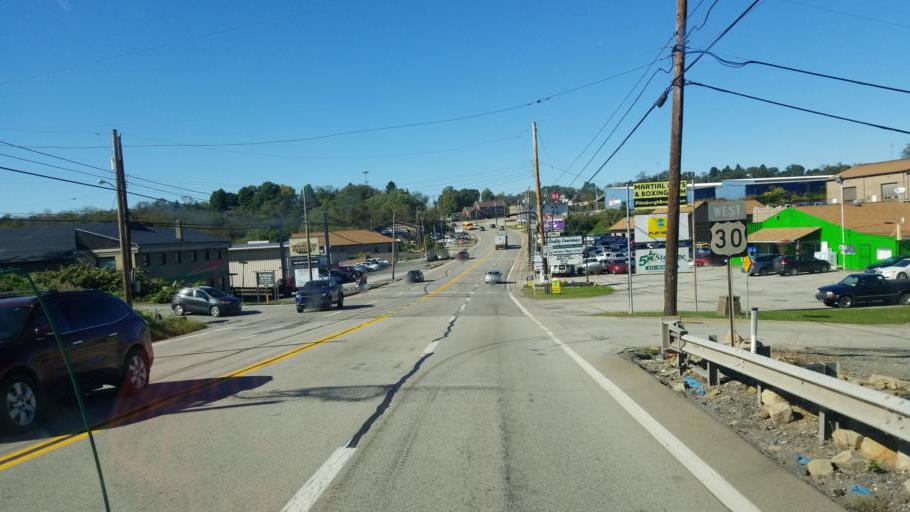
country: US
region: Pennsylvania
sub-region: Westmoreland County
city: Trafford
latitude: 40.3632
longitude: -79.7729
